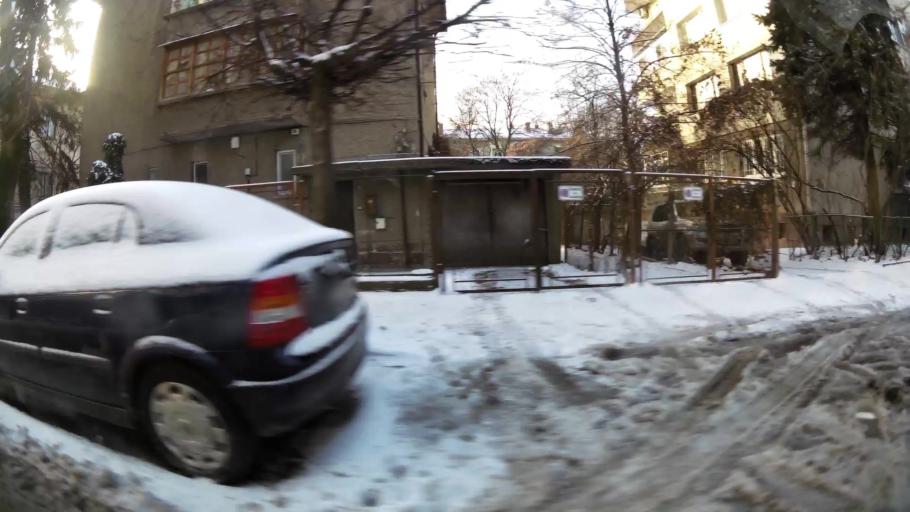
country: BG
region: Sofia-Capital
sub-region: Stolichna Obshtina
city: Sofia
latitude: 42.6711
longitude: 23.3271
